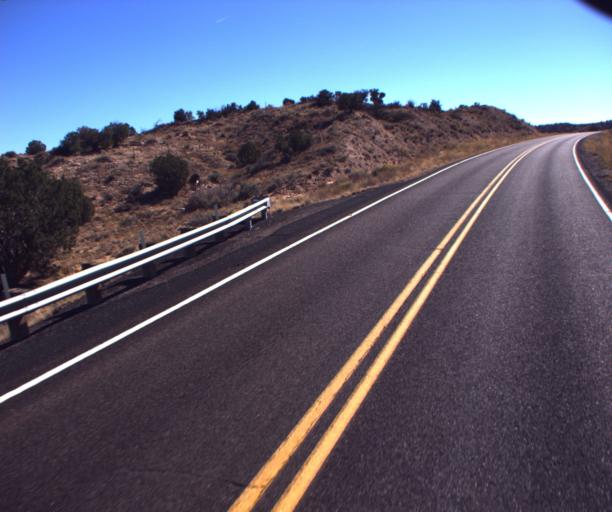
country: US
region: Arizona
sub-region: Navajo County
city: First Mesa
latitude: 35.7433
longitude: -110.1202
